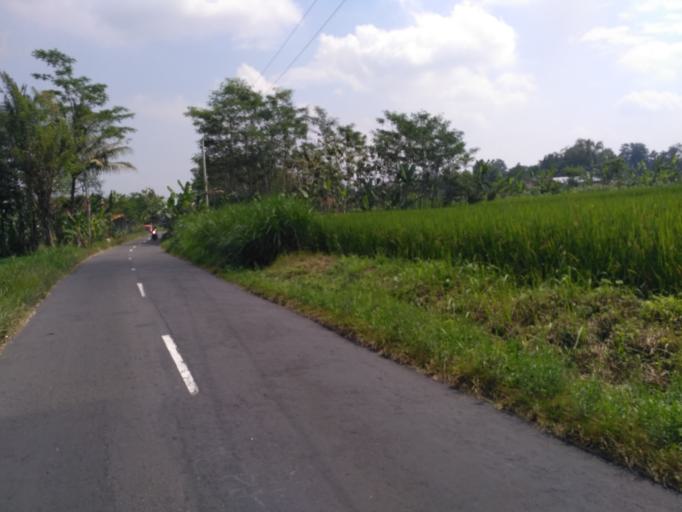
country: ID
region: Daerah Istimewa Yogyakarta
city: Depok
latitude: -7.7189
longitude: 110.4202
